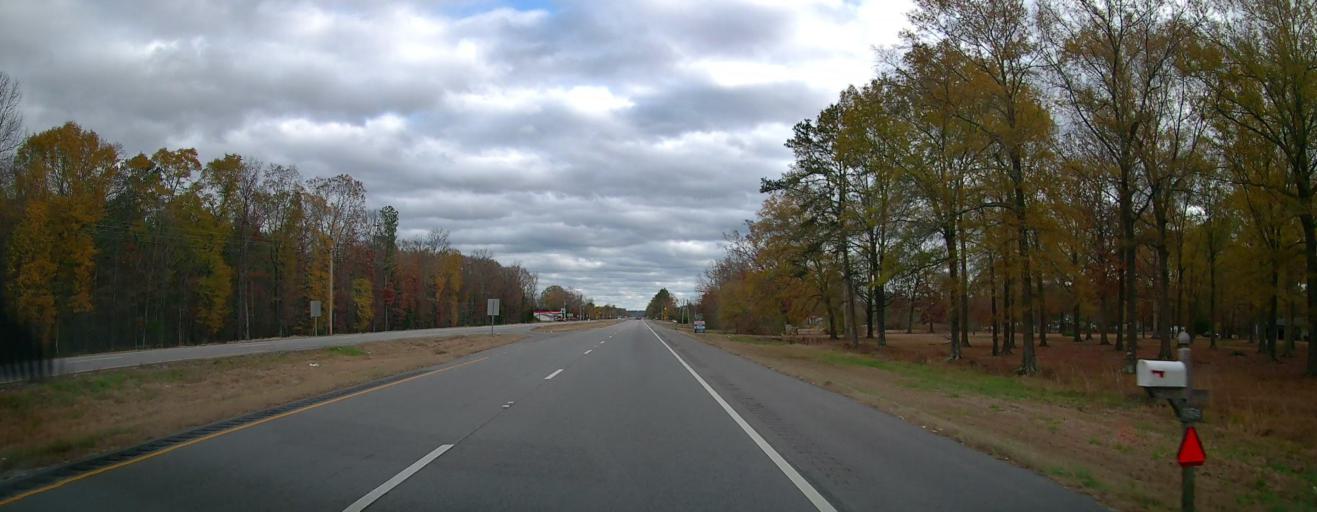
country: US
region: Alabama
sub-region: Lawrence County
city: Town Creek
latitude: 34.6561
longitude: -87.5339
